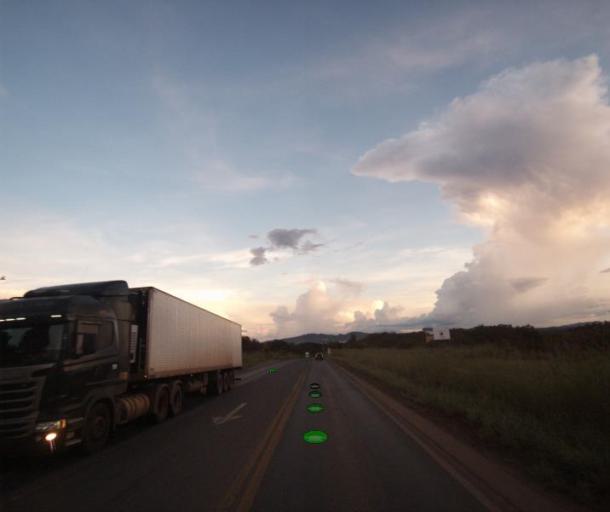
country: BR
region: Goias
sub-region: Uruacu
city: Uruacu
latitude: -14.4794
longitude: -49.1545
